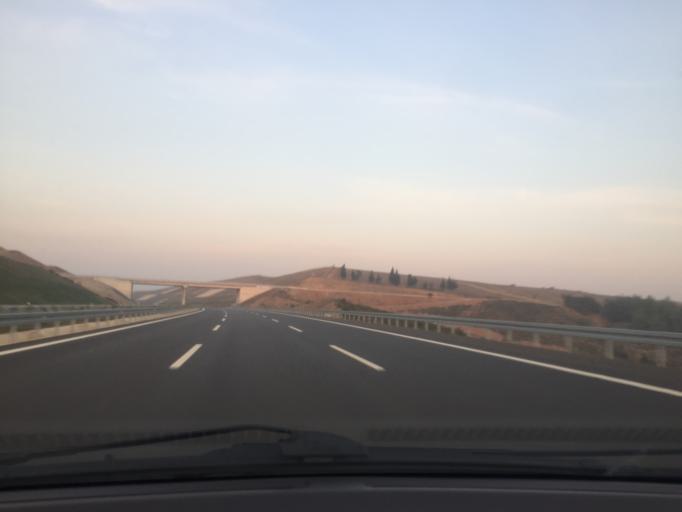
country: TR
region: Bursa
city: Mahmudiye
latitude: 40.2764
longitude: 28.5451
